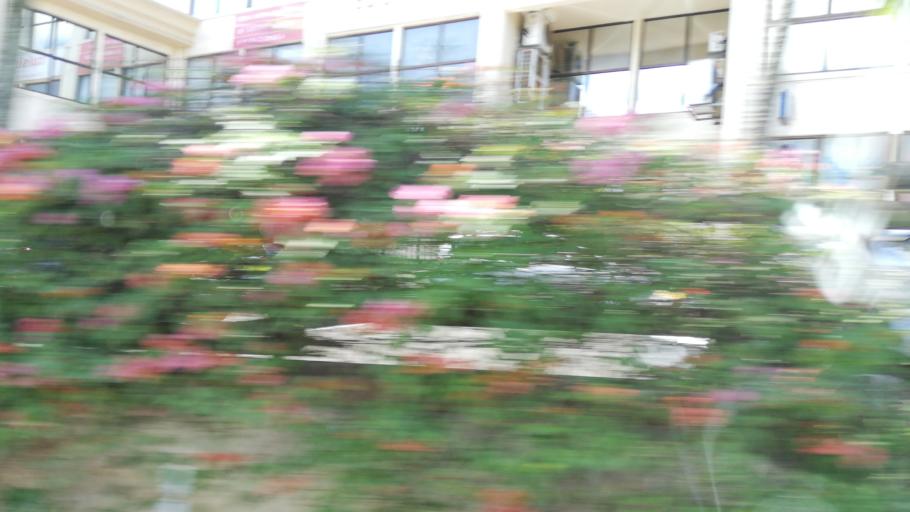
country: MU
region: Plaines Wilhems
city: Ebene
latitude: -20.2318
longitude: 57.4712
